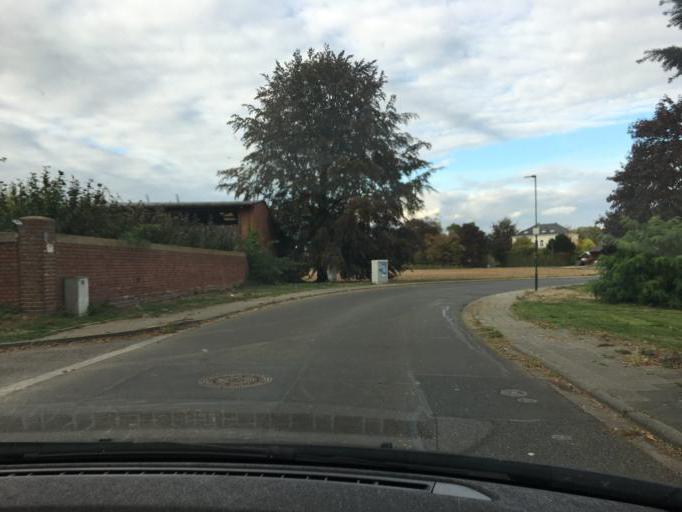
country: DE
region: North Rhine-Westphalia
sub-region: Regierungsbezirk Koln
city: Merzenich
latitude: 50.8596
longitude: 6.5769
